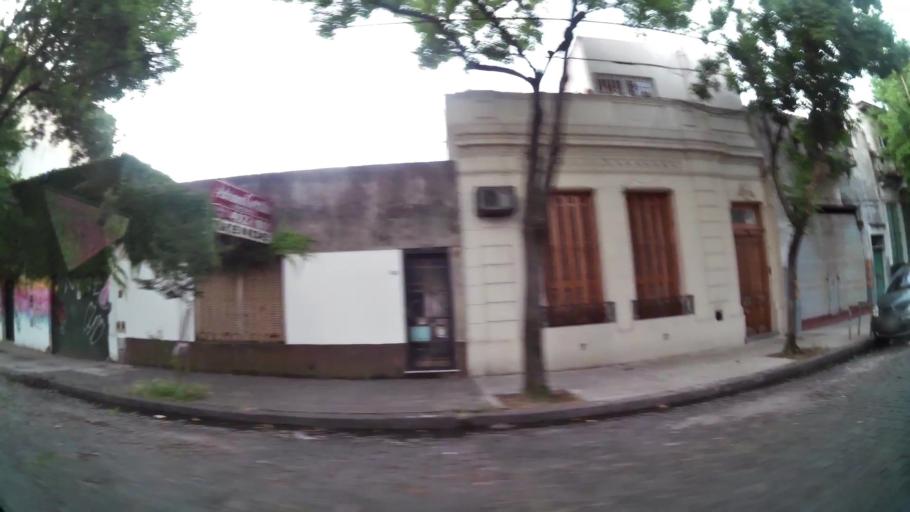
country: AR
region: Buenos Aires F.D.
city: Buenos Aires
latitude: -34.6345
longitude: -58.4197
